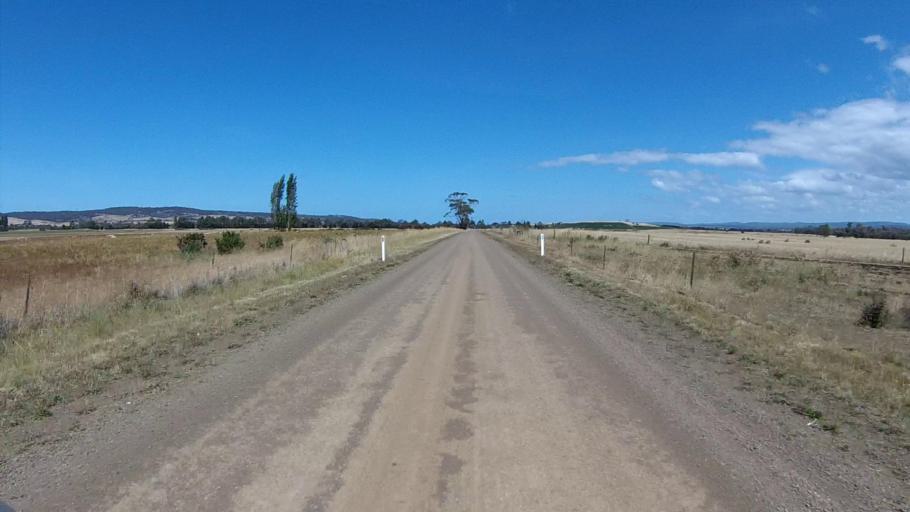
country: AU
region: Tasmania
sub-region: Break O'Day
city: St Helens
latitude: -41.9938
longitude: 148.0671
